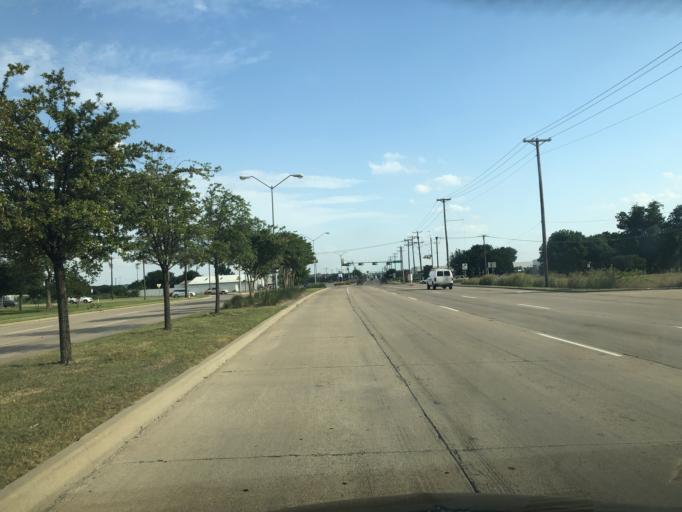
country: US
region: Texas
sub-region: Dallas County
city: Grand Prairie
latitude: 32.7791
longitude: -96.9947
